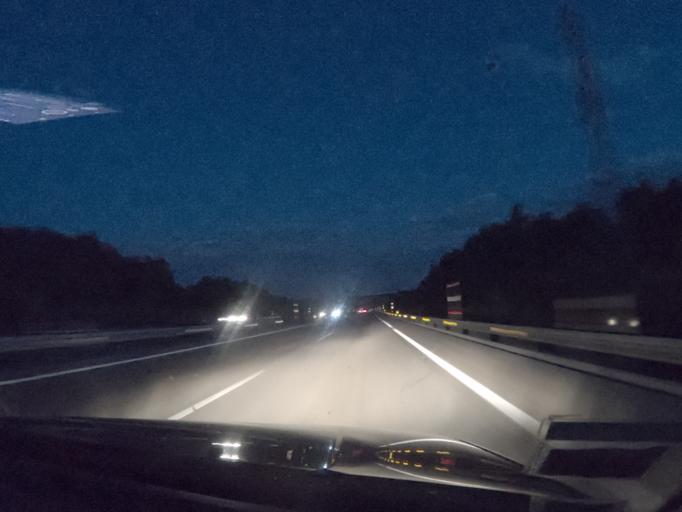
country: ES
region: Castille and Leon
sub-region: Provincia de Leon
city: Brazuelo
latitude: 42.5535
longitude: -6.1821
